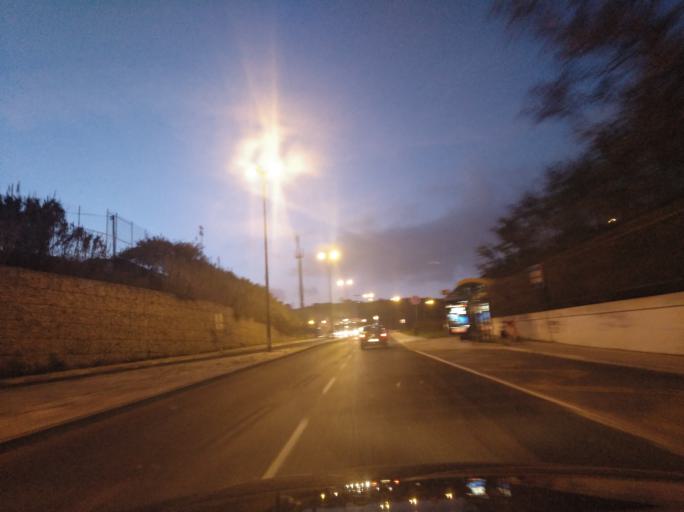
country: PT
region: Lisbon
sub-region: Lisbon
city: Lisbon
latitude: 38.7216
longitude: -9.1197
